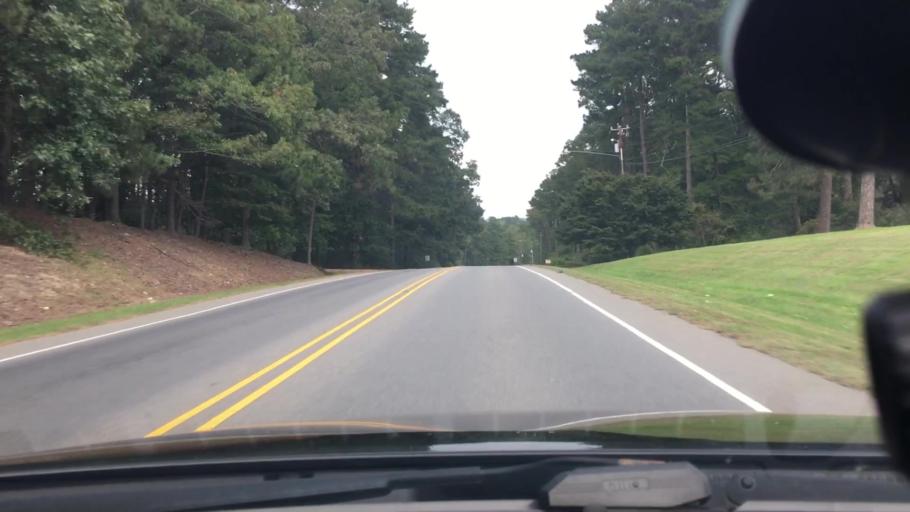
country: US
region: North Carolina
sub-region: Montgomery County
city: Troy
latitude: 35.3604
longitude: -79.8815
